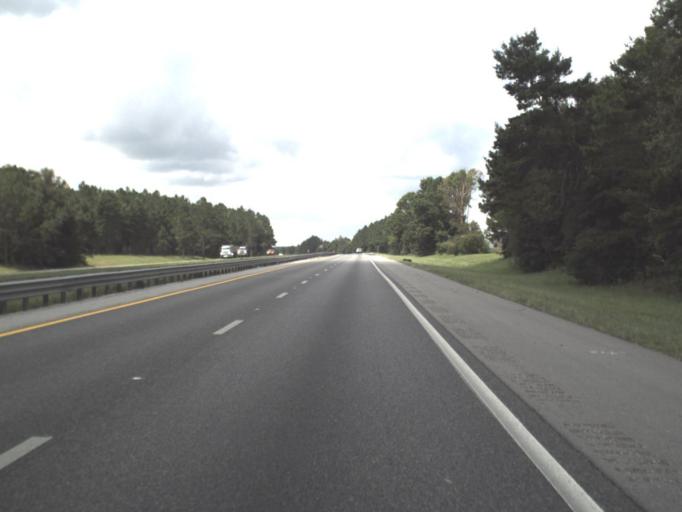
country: US
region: Florida
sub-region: Hernando County
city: Hill 'n Dale
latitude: 28.5058
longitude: -82.2447
